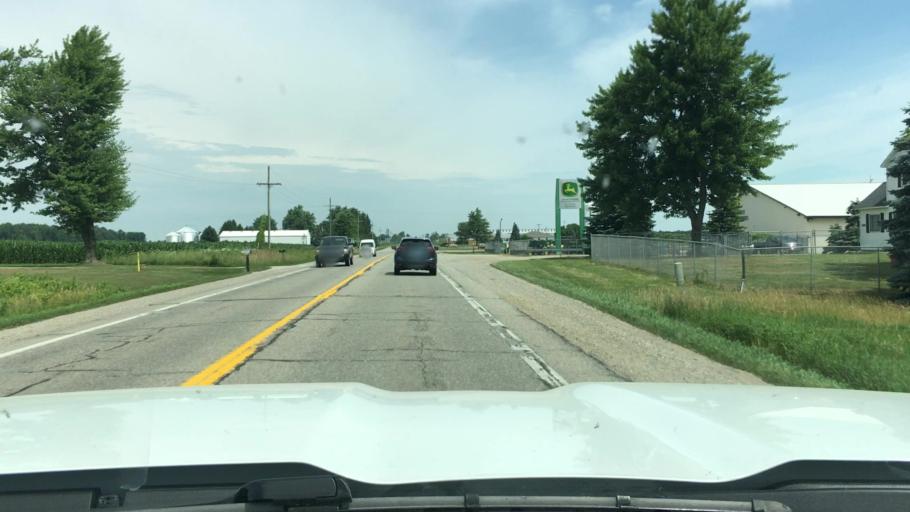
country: US
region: Michigan
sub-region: Sanilac County
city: Marlette
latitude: 43.2531
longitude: -83.0793
